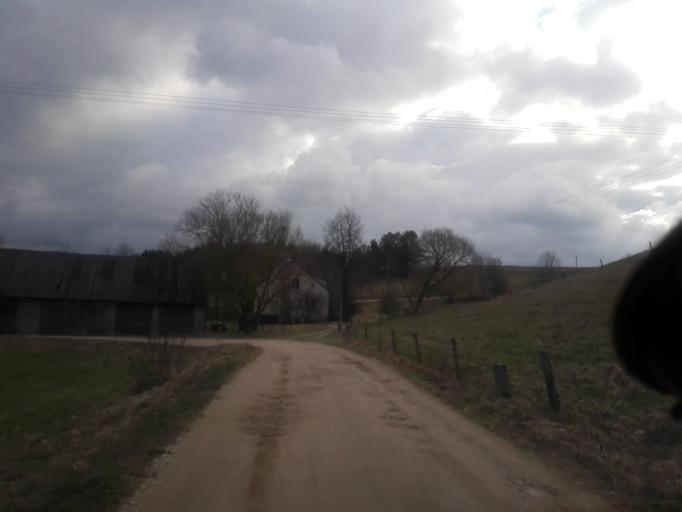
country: PL
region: Podlasie
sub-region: Suwalki
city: Suwalki
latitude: 54.2191
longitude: 22.8093
